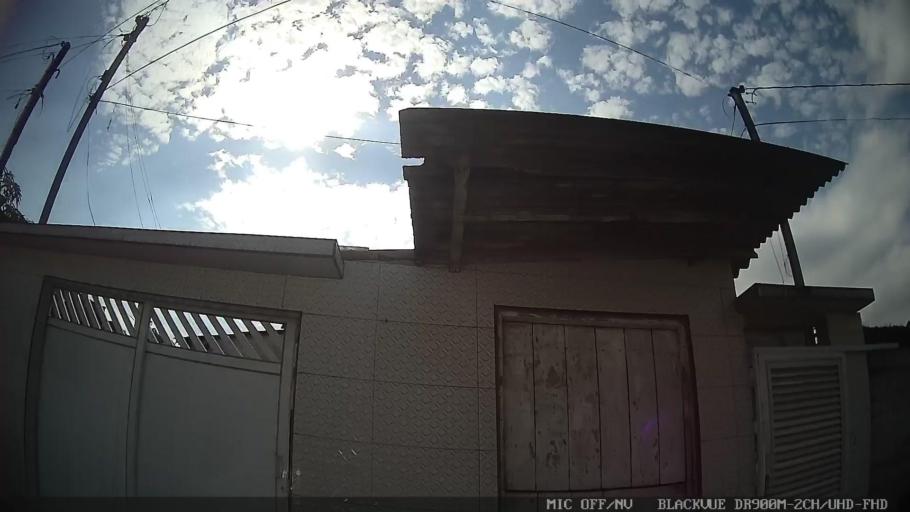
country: BR
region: Sao Paulo
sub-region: Santos
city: Santos
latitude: -23.9511
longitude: -46.3004
